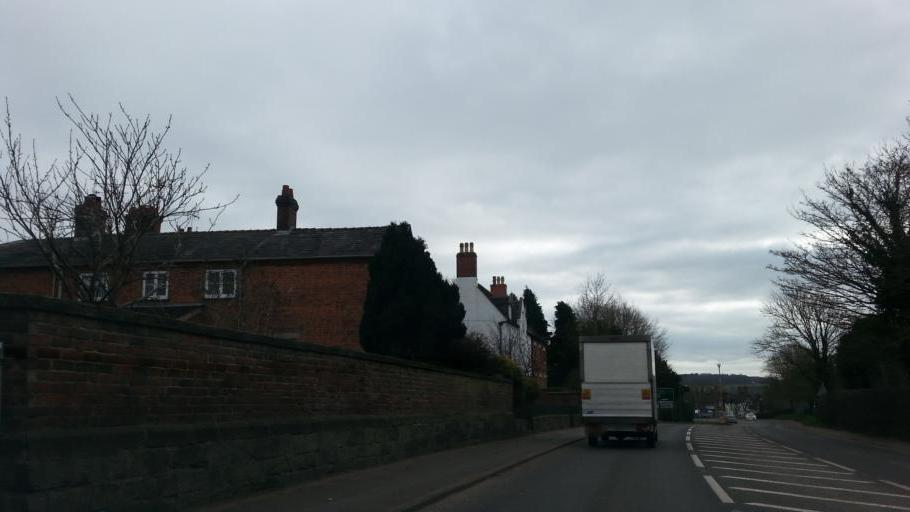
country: GB
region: England
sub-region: Staffordshire
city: Stafford
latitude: 52.8635
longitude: -2.0788
